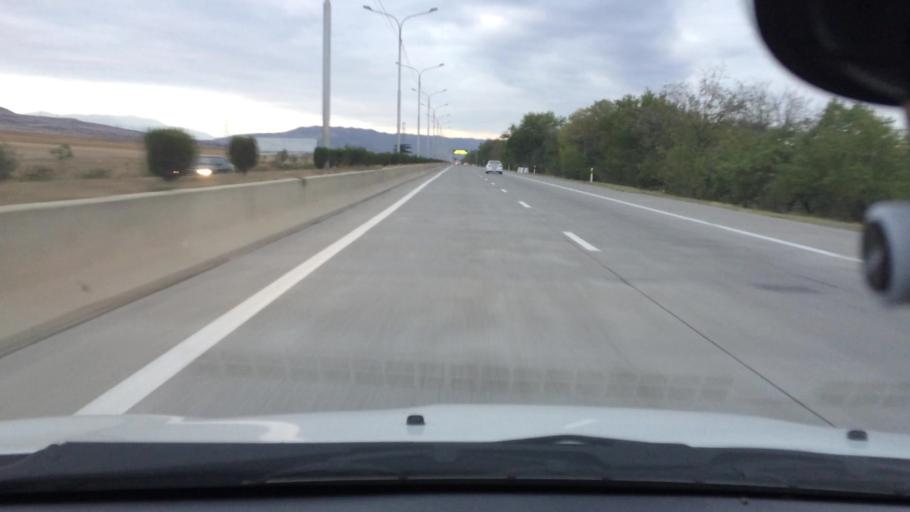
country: GE
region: Mtskheta-Mtianeti
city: Mtskheta
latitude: 41.8959
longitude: 44.6340
